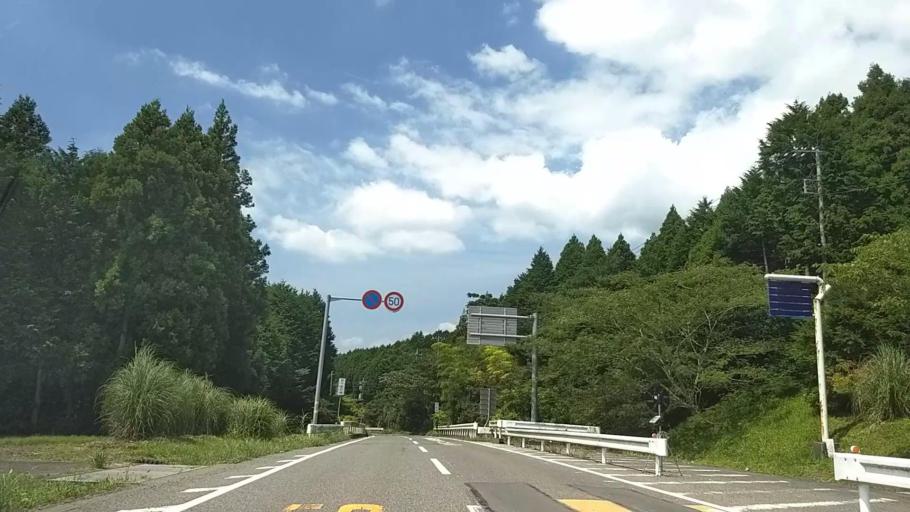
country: JP
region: Shizuoka
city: Fuji
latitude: 35.2484
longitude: 138.7093
